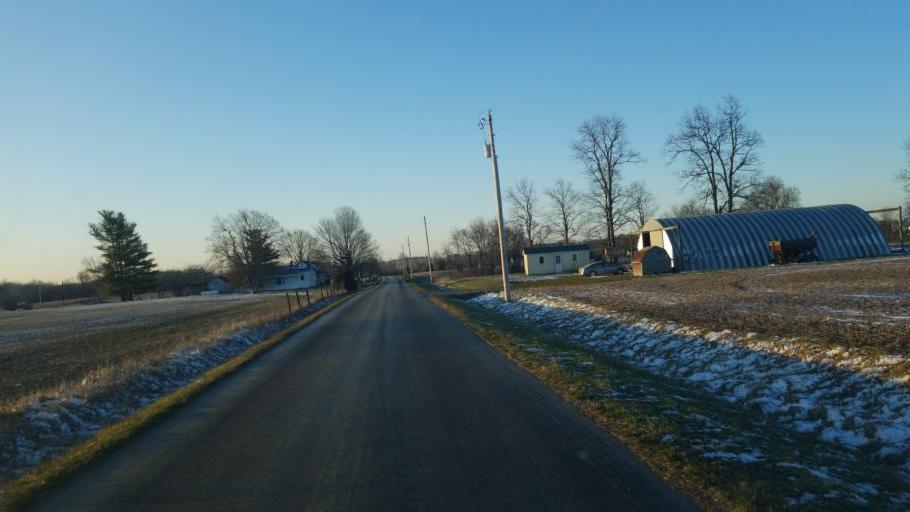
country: US
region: Ohio
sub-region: Highland County
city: Leesburg
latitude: 39.2707
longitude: -83.5038
